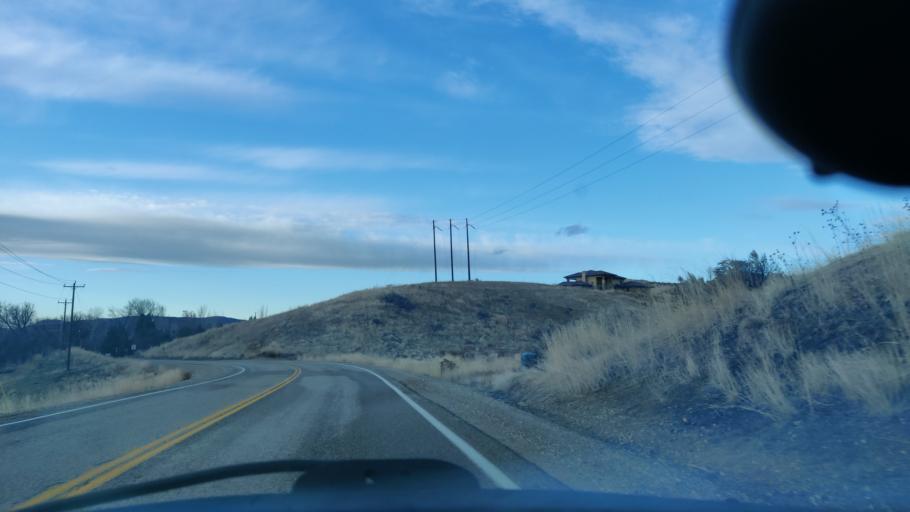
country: US
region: Idaho
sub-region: Ada County
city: Garden City
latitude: 43.7268
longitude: -116.2506
